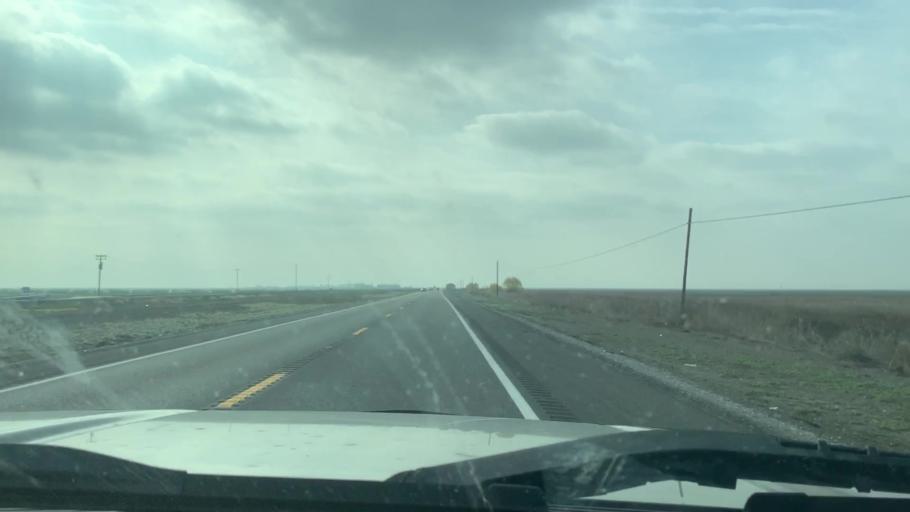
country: US
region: California
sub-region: Kings County
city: Stratford
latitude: 36.1565
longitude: -119.8569
